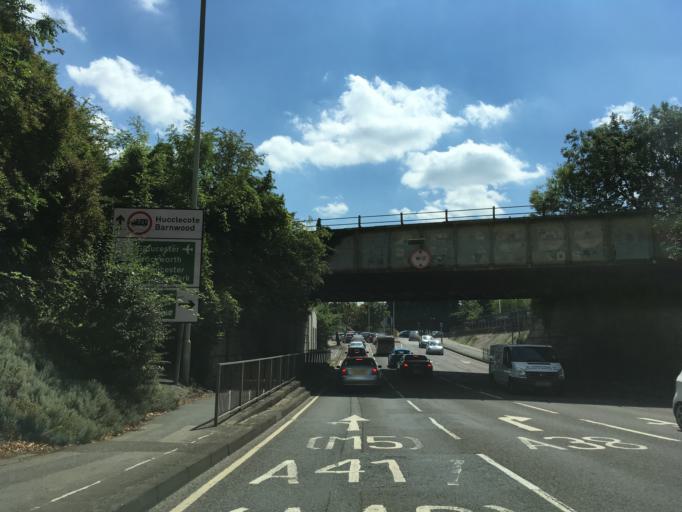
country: GB
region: England
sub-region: Gloucestershire
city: Barnwood
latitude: 51.8649
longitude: -2.2152
